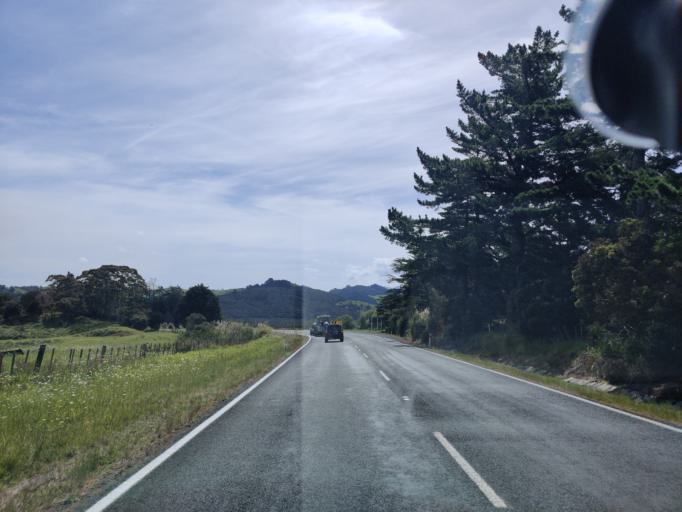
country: NZ
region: Northland
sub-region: Far North District
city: Kaitaia
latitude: -35.4565
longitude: 173.4744
